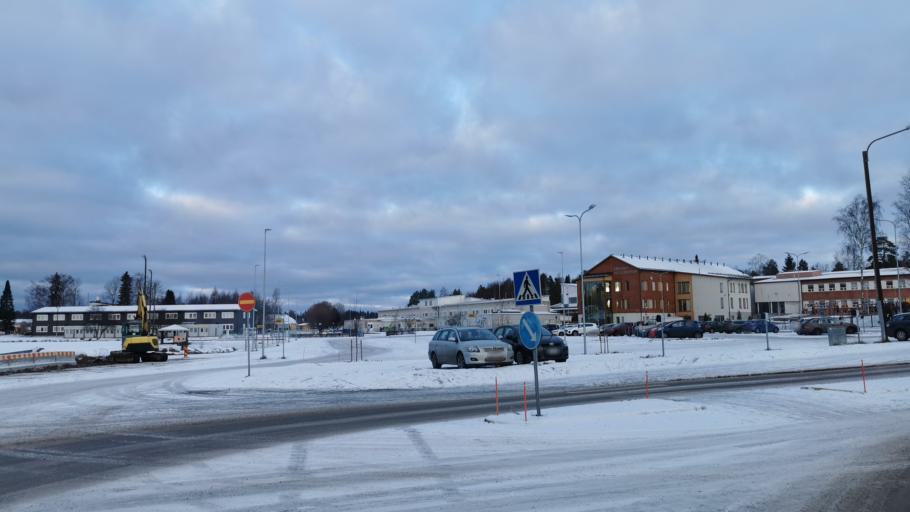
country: FI
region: Ostrobothnia
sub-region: Vaasa
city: Korsholm
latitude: 63.1157
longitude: 21.6855
